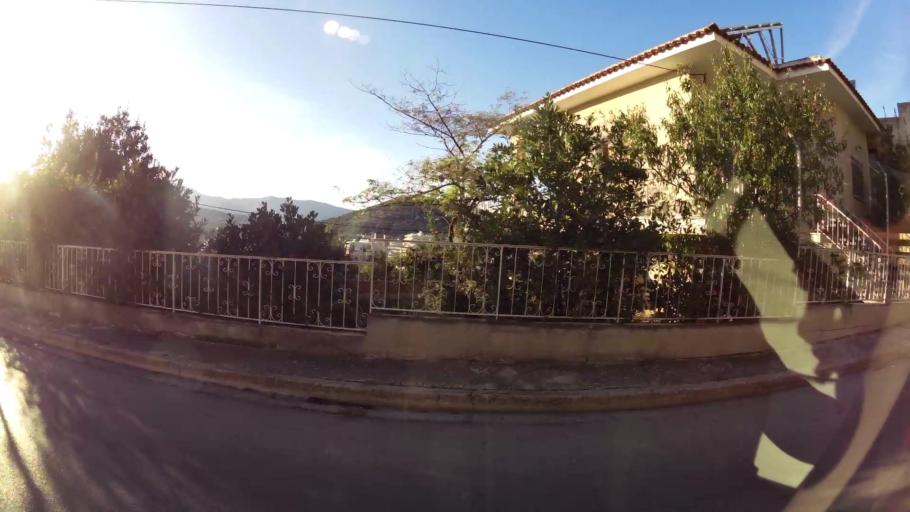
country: GR
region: Attica
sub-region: Nomarchia Anatolikis Attikis
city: Spata
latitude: 37.9615
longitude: 23.9093
